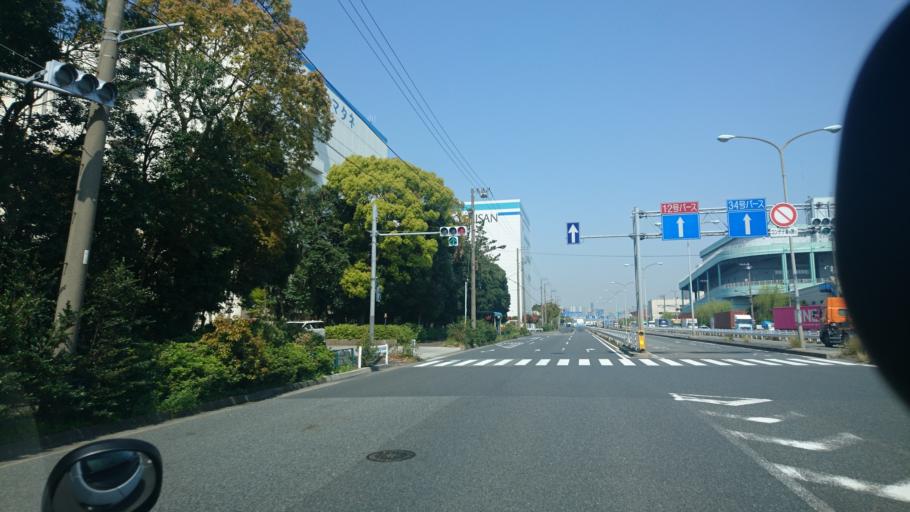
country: JP
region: Kanagawa
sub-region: Kawasaki-shi
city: Kawasaki
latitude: 35.5924
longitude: 139.7670
